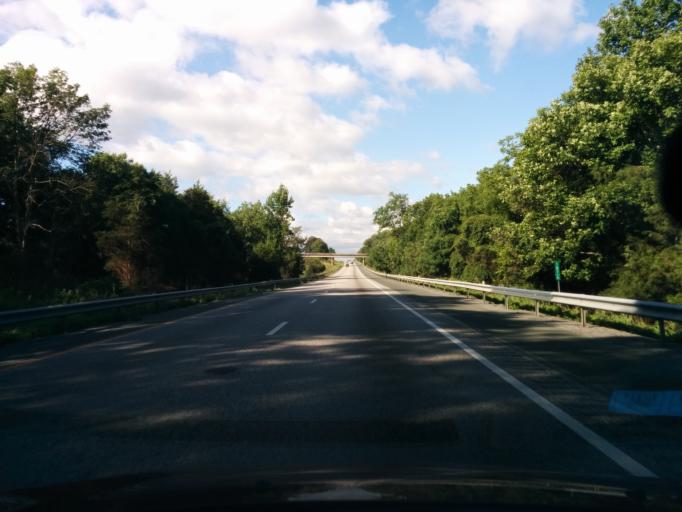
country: US
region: Virginia
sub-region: City of Lexington
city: Lexington
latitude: 37.7434
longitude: -79.4207
